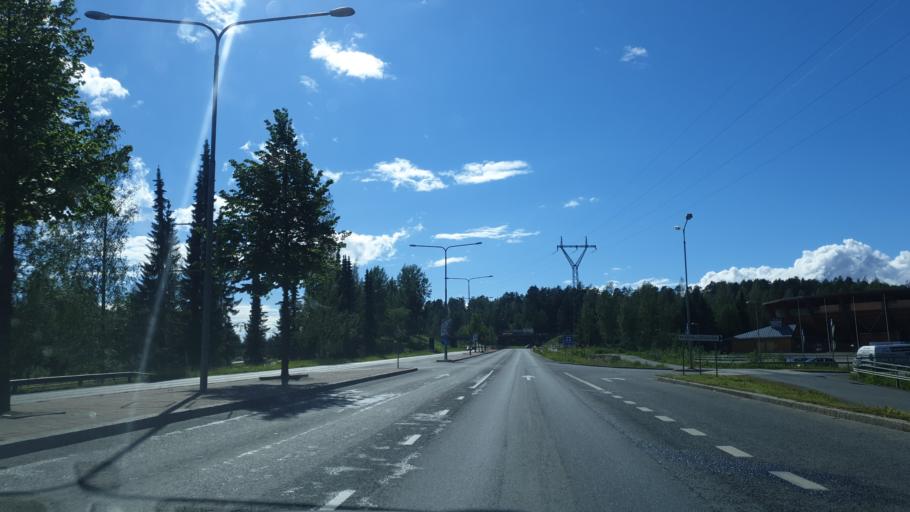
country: FI
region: Northern Savo
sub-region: Kuopio
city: Kuopio
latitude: 62.9020
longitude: 27.6686
